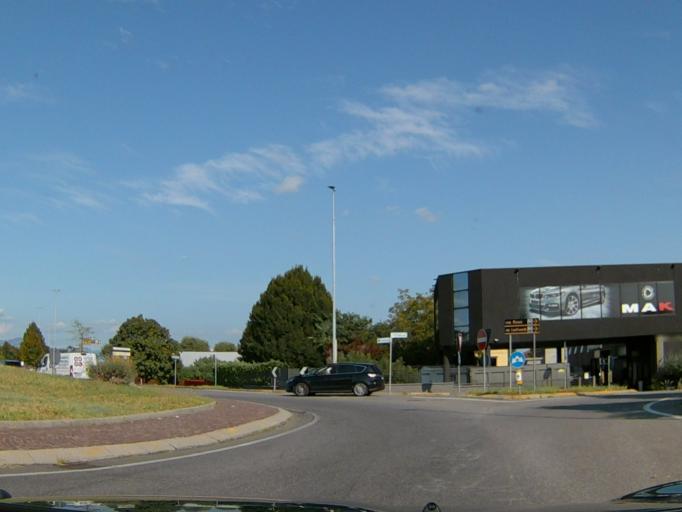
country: IT
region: Lombardy
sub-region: Provincia di Brescia
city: Palazzolo sull'Oglio
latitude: 45.5878
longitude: 9.8916
